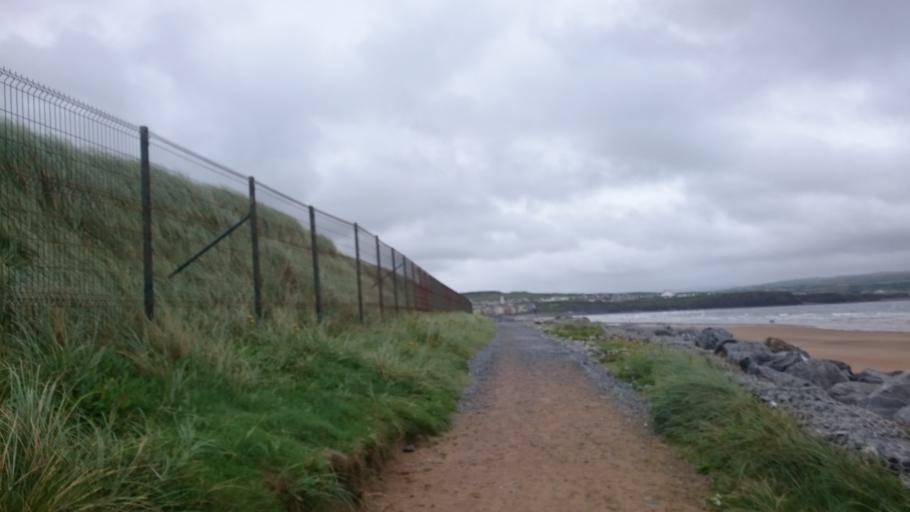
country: IE
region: Munster
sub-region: An Clar
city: Kilrush
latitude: 52.9388
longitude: -9.3560
